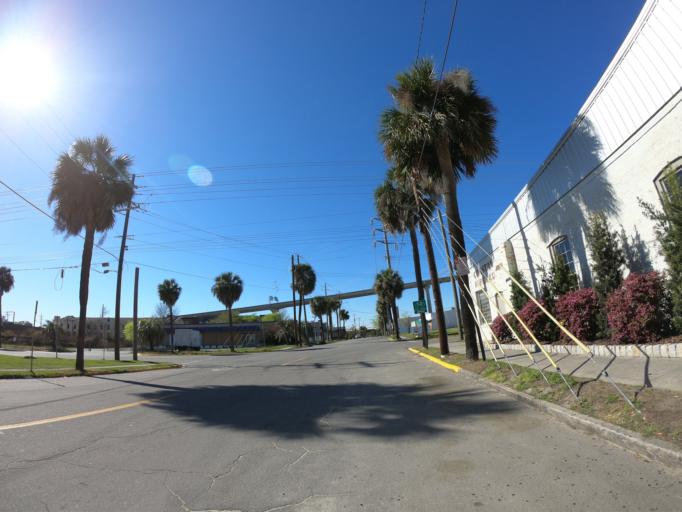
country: US
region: Georgia
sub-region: Chatham County
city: Savannah
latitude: 32.0842
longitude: -81.0987
